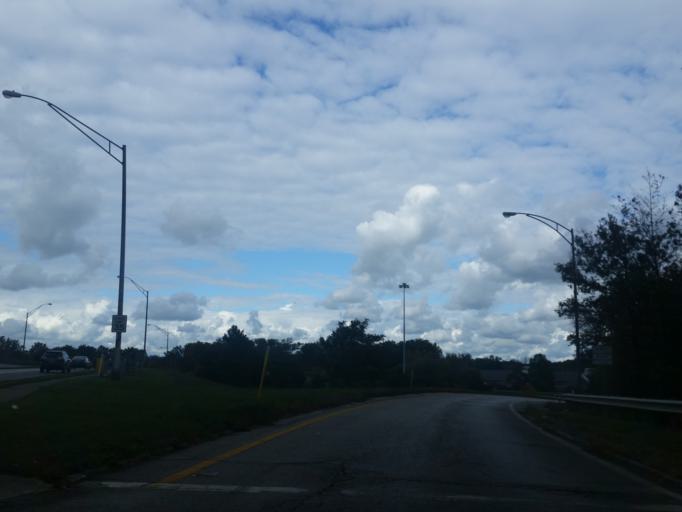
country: US
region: Ohio
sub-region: Cuyahoga County
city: Westlake
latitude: 41.4713
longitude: -81.9015
